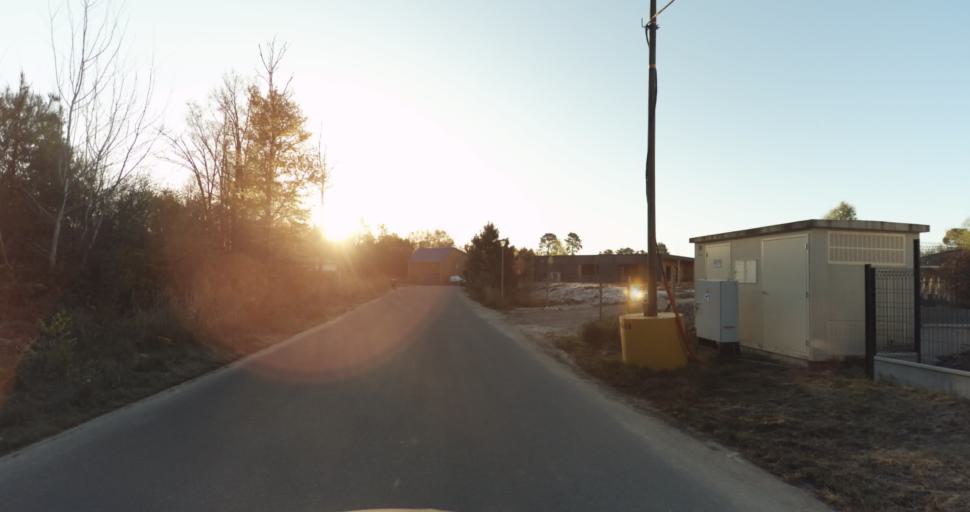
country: FR
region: Aquitaine
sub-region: Departement de la Gironde
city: Martignas-sur-Jalle
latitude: 44.8108
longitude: -0.7689
